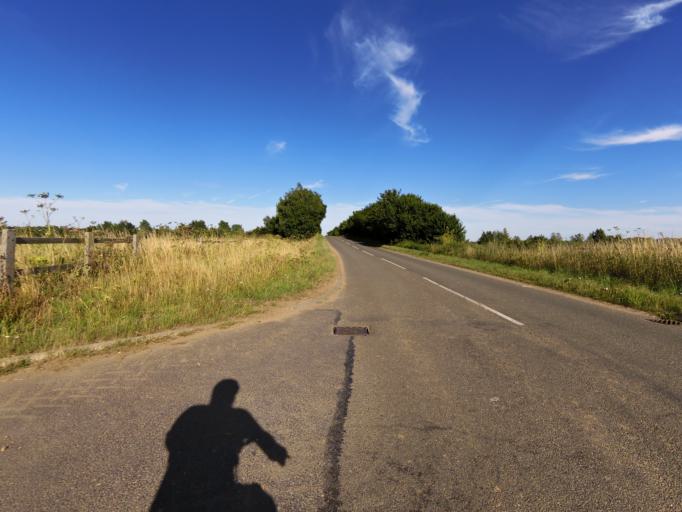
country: GB
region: England
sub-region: Suffolk
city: Kesgrave
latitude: 52.0351
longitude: 1.2565
